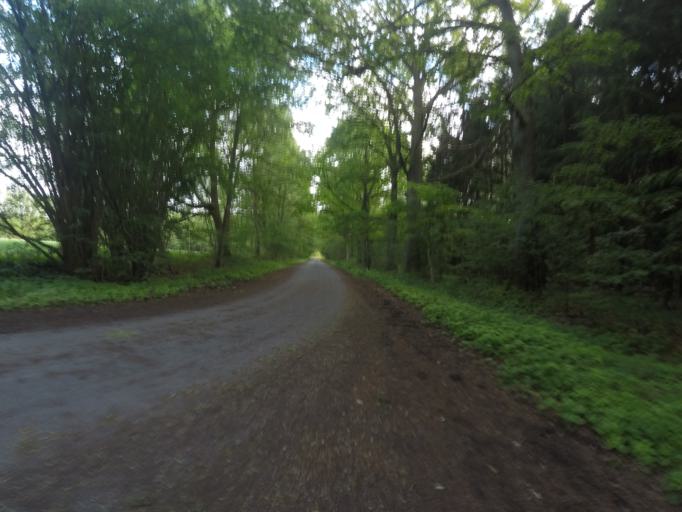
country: DE
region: Schleswig-Holstein
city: Bonningstedt
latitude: 53.6754
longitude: 9.9293
